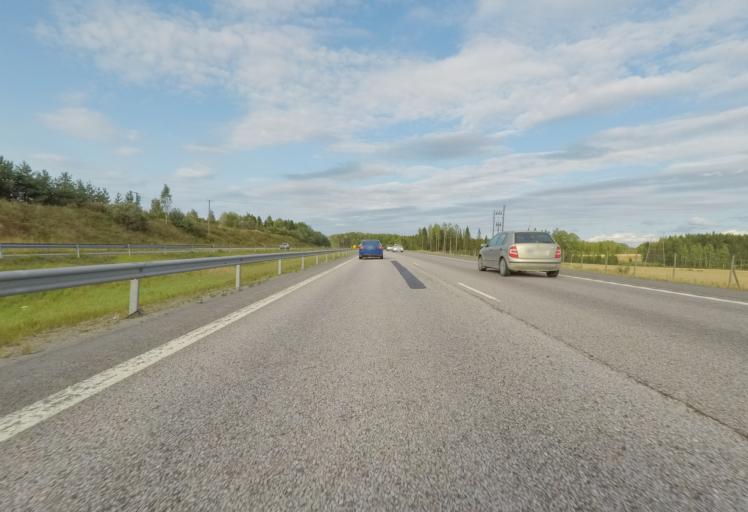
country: FI
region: Paijanne Tavastia
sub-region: Lahti
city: Lahti
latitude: 60.9453
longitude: 25.6784
